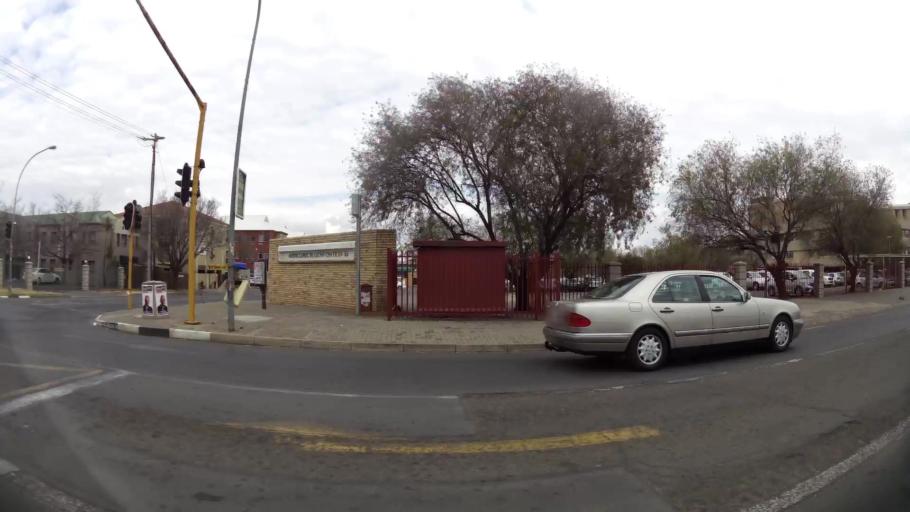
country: ZA
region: Orange Free State
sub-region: Mangaung Metropolitan Municipality
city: Bloemfontein
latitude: -29.1085
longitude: 26.2049
